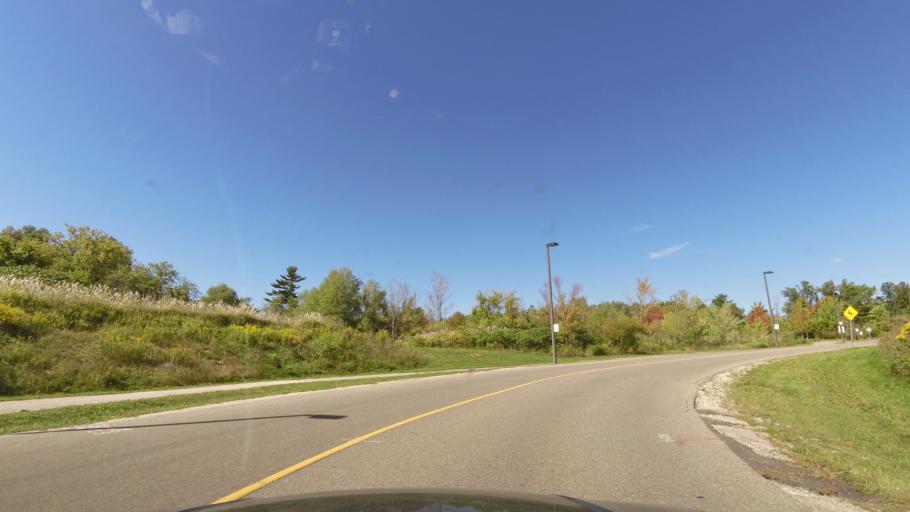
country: CA
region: Ontario
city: Mississauga
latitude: 43.5645
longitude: -79.6703
